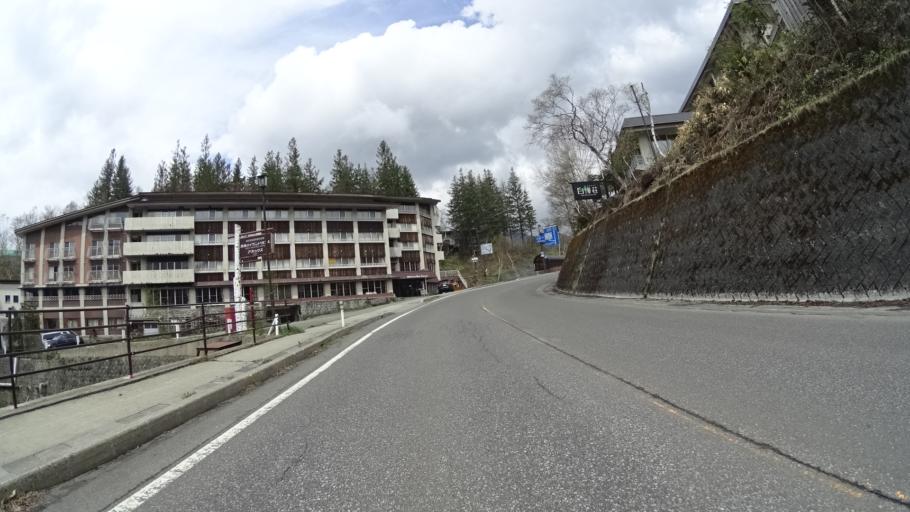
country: JP
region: Nagano
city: Nakano
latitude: 36.7180
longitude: 138.4908
